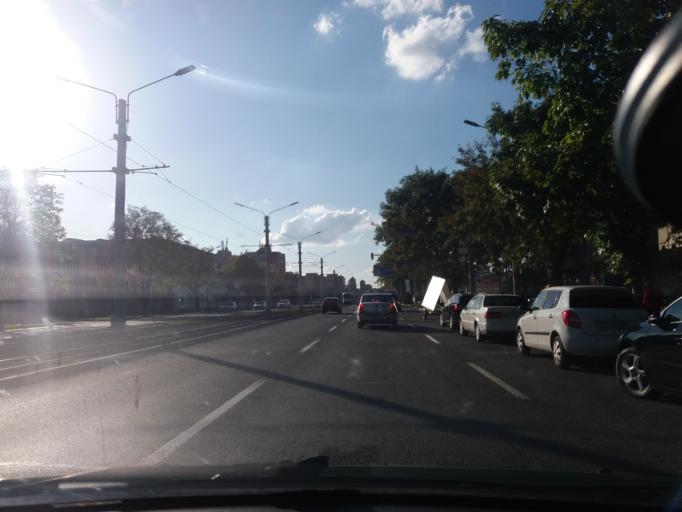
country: RO
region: Arad
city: Arad
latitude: 46.1912
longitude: 21.3138
